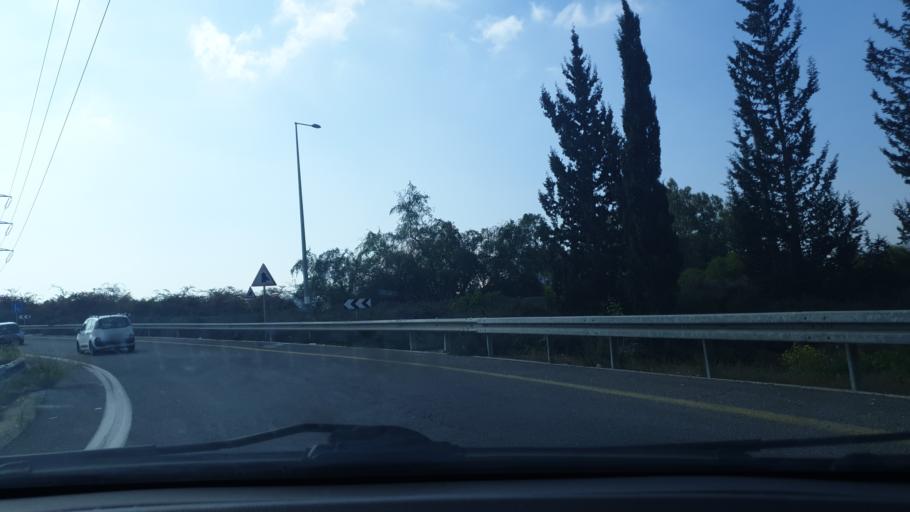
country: IL
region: Tel Aviv
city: Azor
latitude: 32.0119
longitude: 34.8132
